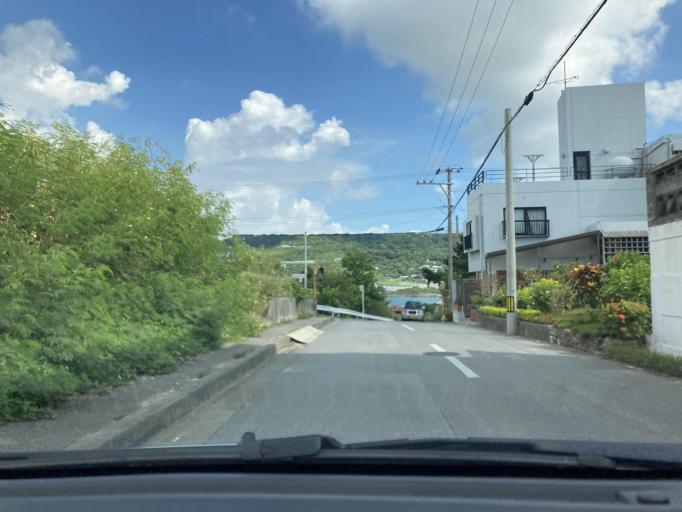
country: JP
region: Okinawa
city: Itoman
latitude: 26.1295
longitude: 127.7741
